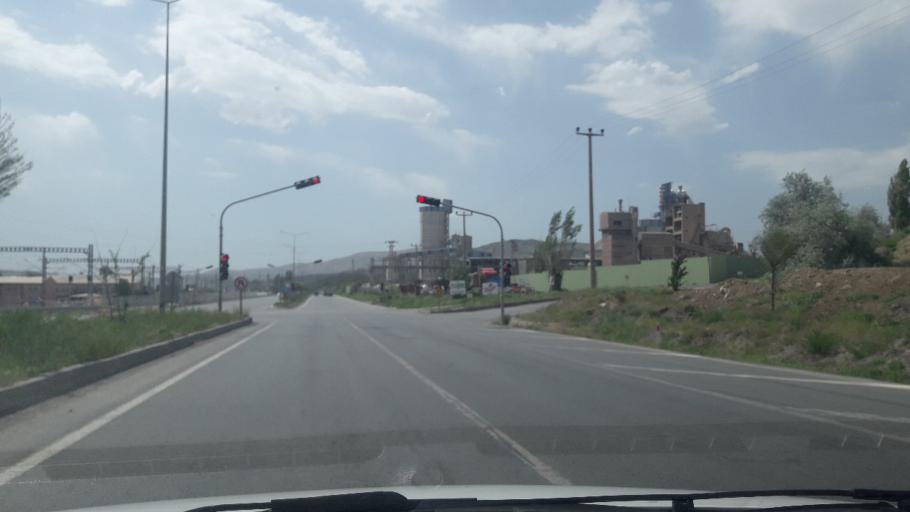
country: TR
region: Sivas
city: Sivas
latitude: 39.7186
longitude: 36.9437
